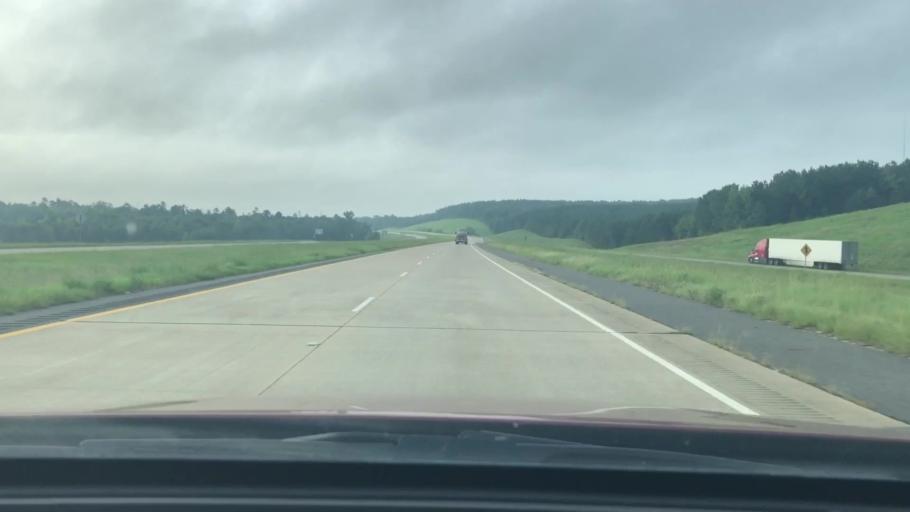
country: US
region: Louisiana
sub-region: Caddo Parish
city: Vivian
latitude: 32.9418
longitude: -93.8978
